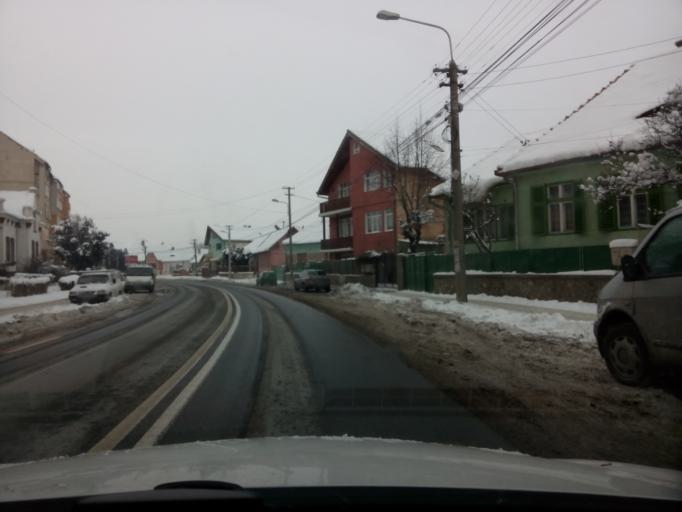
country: RO
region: Sibiu
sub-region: Municipiul Sibiu
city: Sibiu
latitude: 45.8073
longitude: 24.1518
